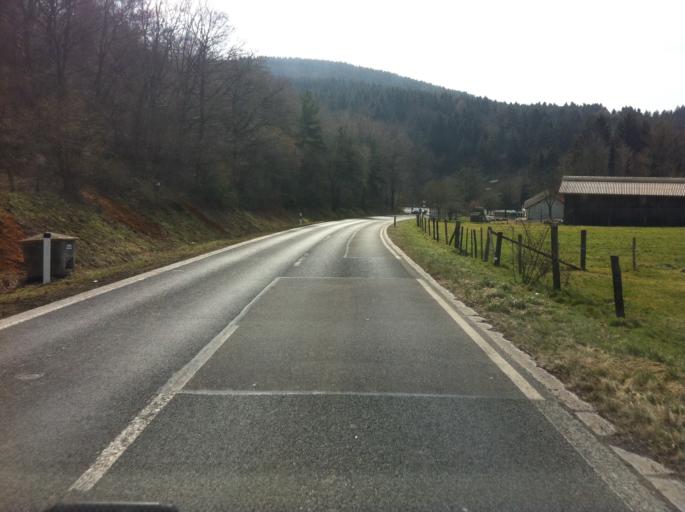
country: DE
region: Rheinland-Pfalz
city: Hummel
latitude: 50.5076
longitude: 6.8014
